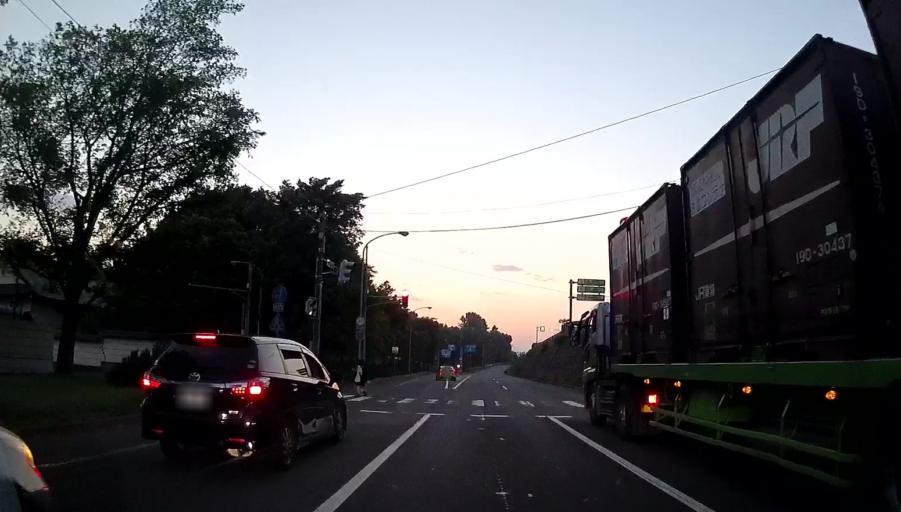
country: JP
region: Hokkaido
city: Sapporo
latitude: 43.0246
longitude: 141.4525
